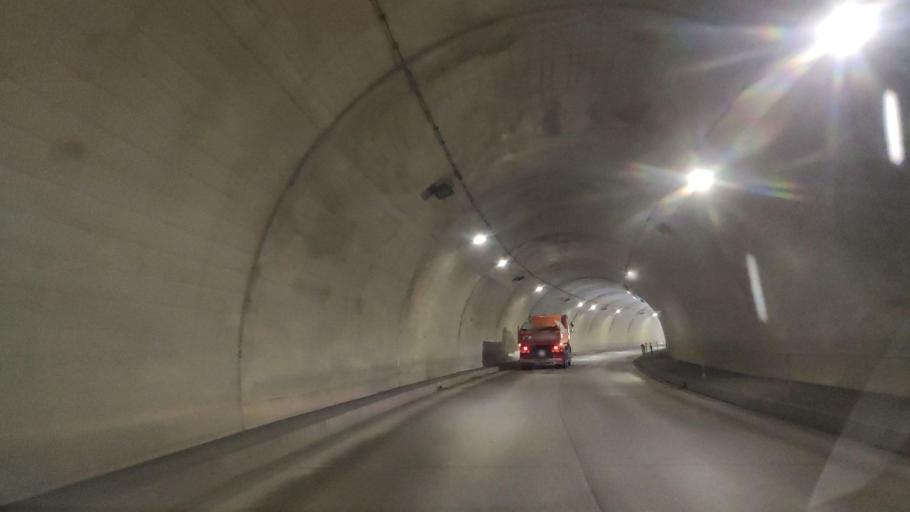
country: JP
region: Nagano
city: Iiyama
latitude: 36.9106
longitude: 138.3163
